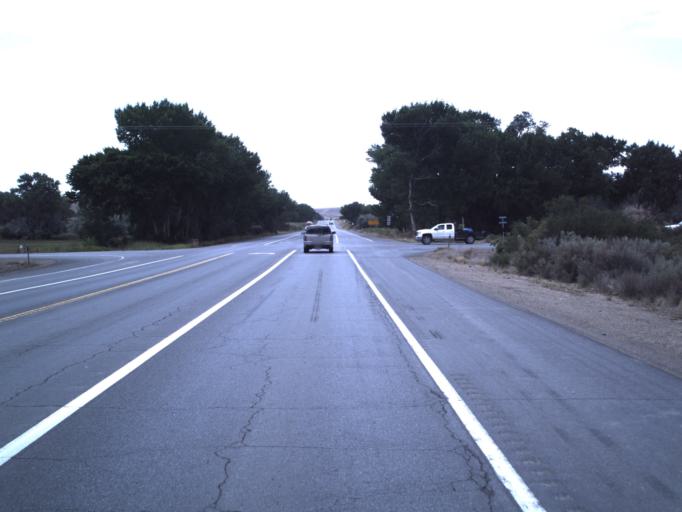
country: US
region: Utah
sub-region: Duchesne County
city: Duchesne
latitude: 40.1541
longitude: -110.2178
